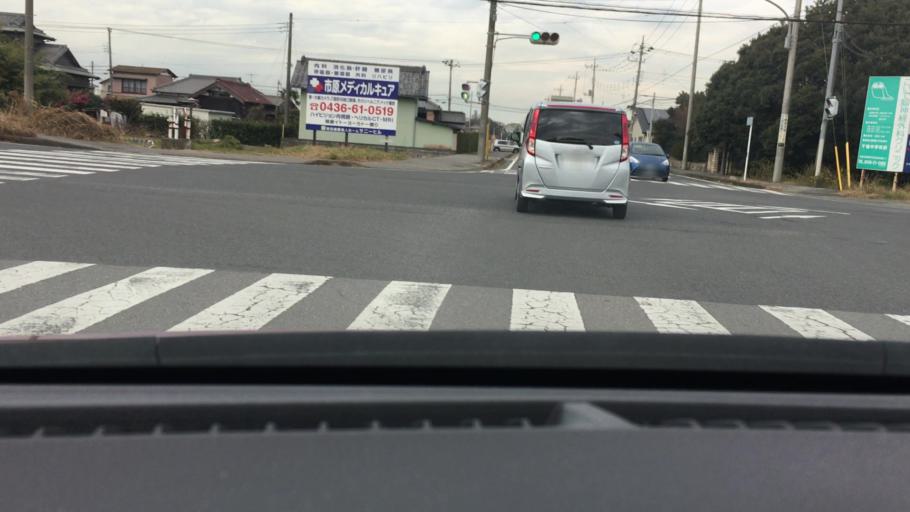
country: JP
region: Chiba
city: Ichihara
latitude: 35.4778
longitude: 140.0608
